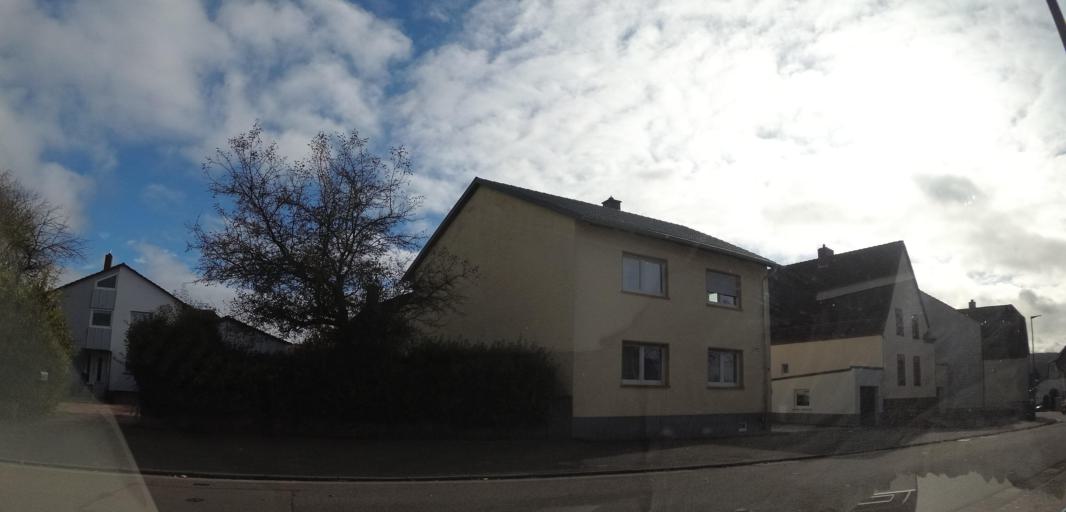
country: DE
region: Rheinland-Pfalz
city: Hutschenhausen
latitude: 49.4219
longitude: 7.4851
